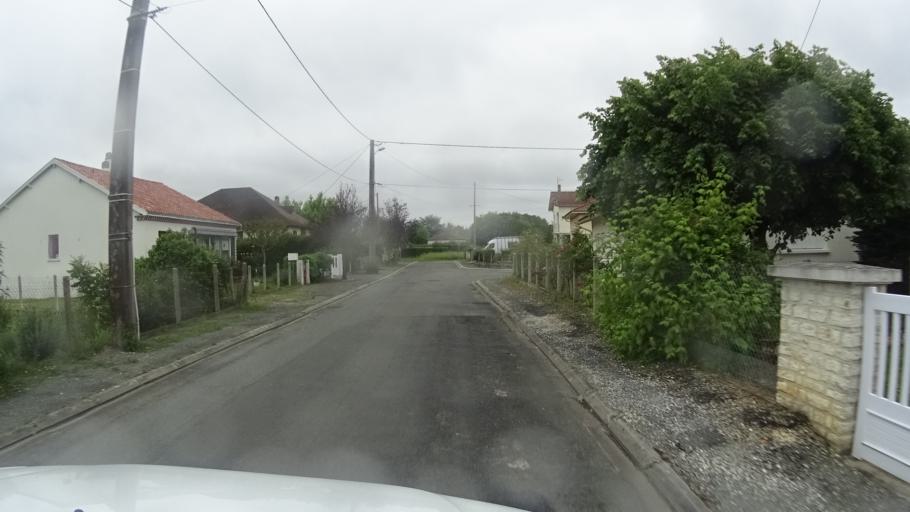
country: FR
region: Aquitaine
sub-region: Departement de la Dordogne
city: Mussidan
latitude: 45.0322
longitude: 0.3652
